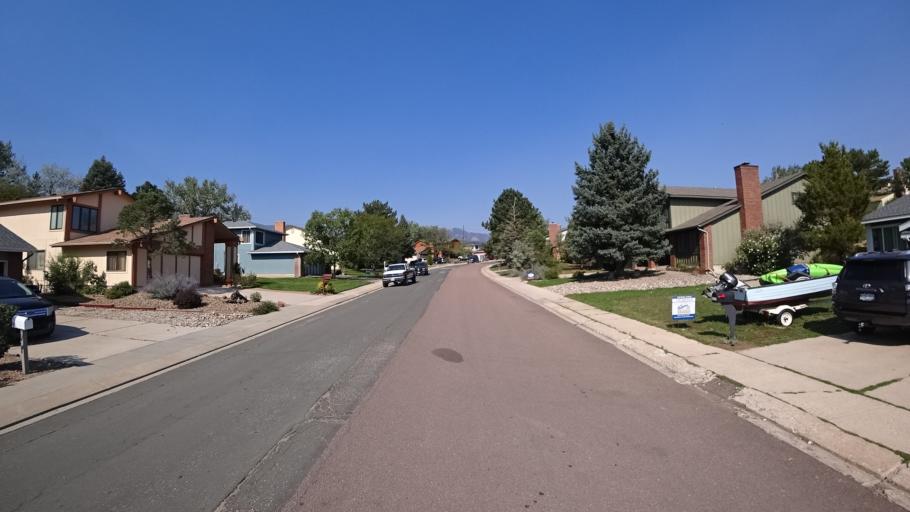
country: US
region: Colorado
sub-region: El Paso County
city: Stratmoor
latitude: 38.7849
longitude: -104.8188
